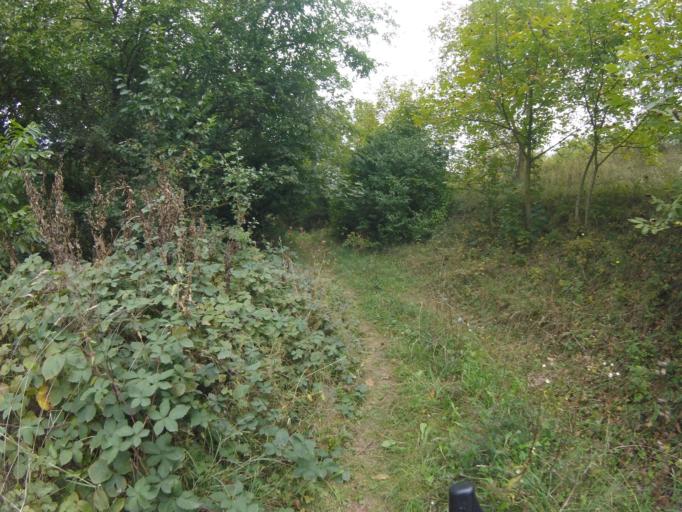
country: HU
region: Pest
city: Szob
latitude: 47.8289
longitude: 18.8140
